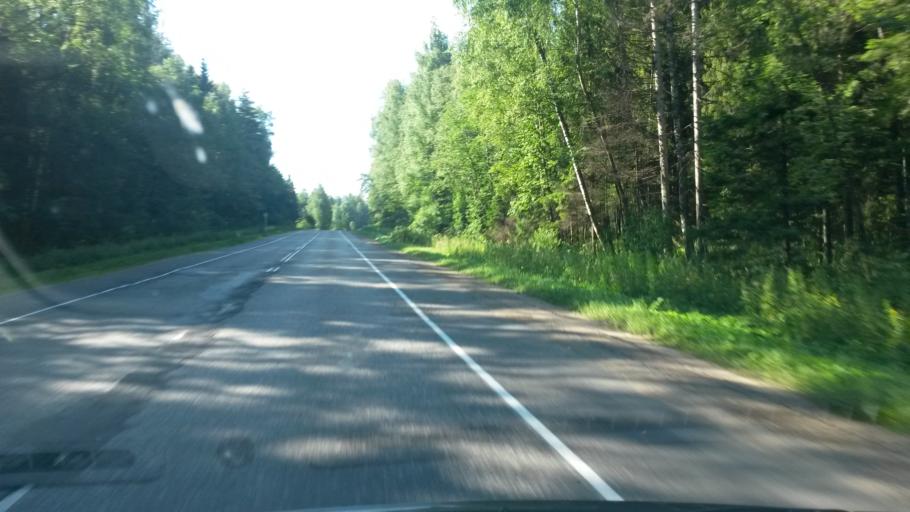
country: RU
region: Ivanovo
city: Pistsovo
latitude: 57.1116
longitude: 40.6490
